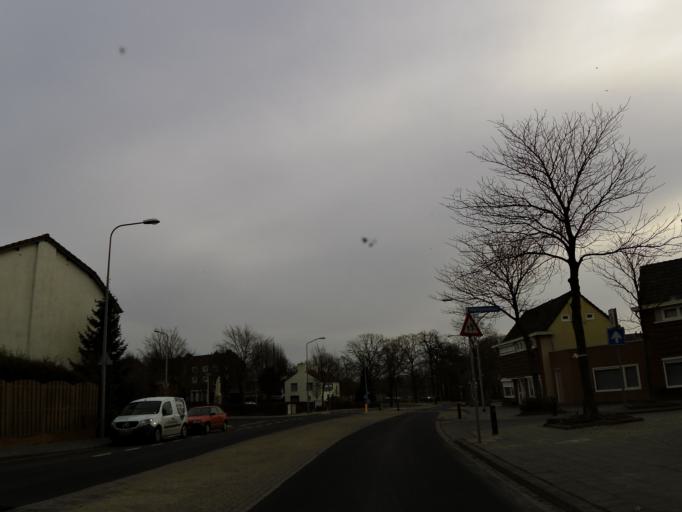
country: NL
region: Limburg
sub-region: Gemeente Heerlen
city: Hoensbroek
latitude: 50.9185
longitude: 5.9135
